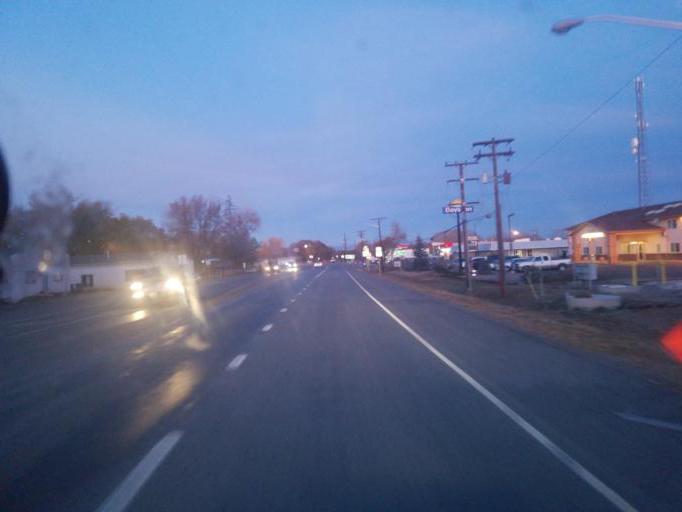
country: US
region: Colorado
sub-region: Alamosa County
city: Alamosa East
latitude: 37.4732
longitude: -105.8546
